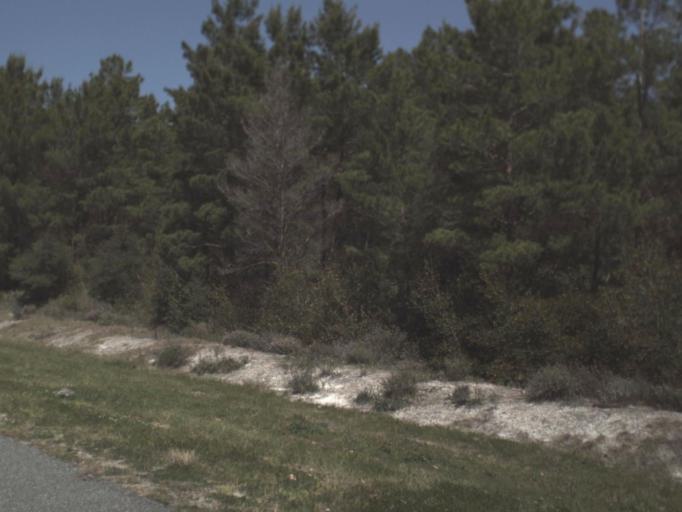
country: US
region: Florida
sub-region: Gulf County
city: Port Saint Joe
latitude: 29.8768
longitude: -85.3402
